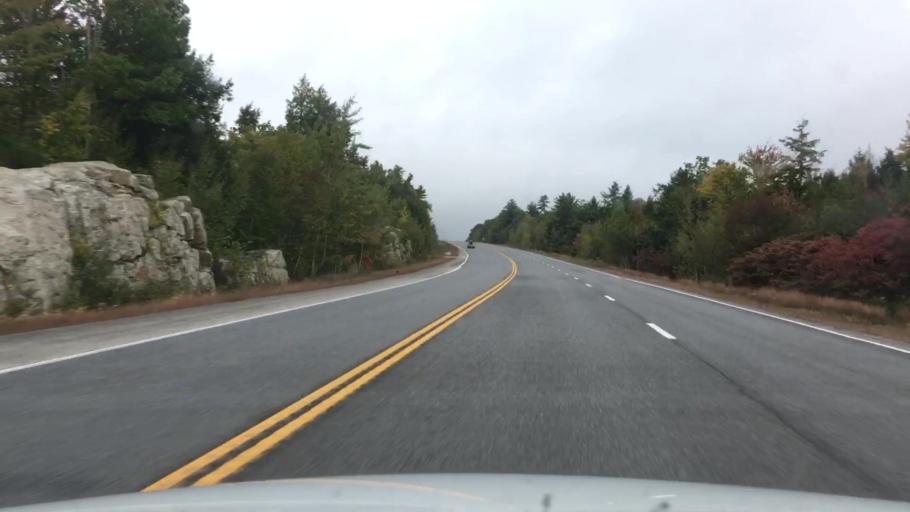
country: US
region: Maine
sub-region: Cumberland County
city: New Gloucester
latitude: 43.9555
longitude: -70.3521
